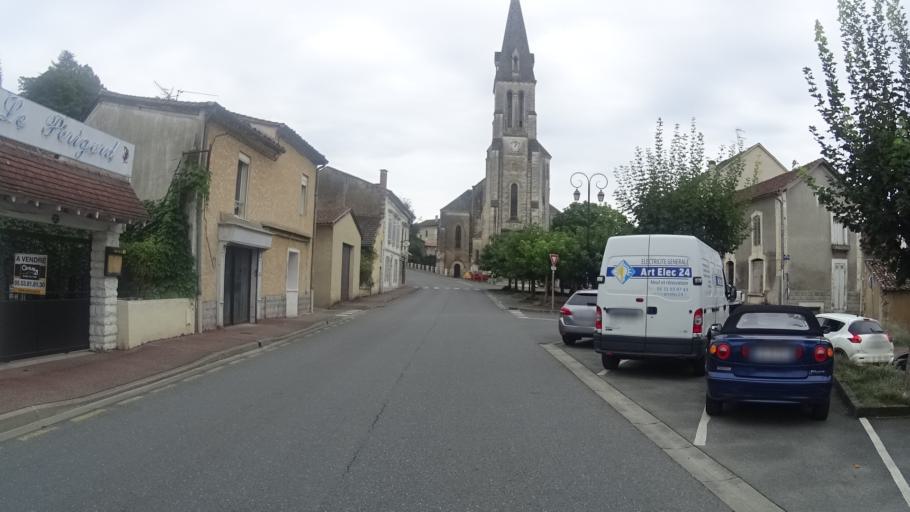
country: FR
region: Aquitaine
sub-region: Departement de la Dordogne
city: Mussidan
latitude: 45.0356
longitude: 0.3691
